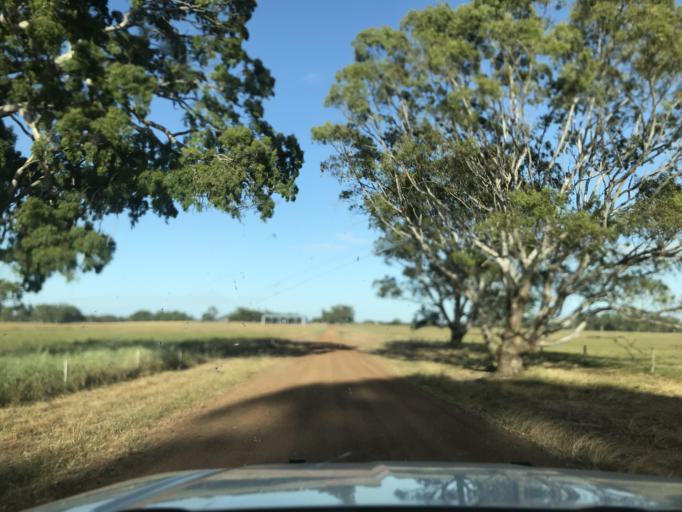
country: AU
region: South Australia
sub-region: Naracoorte and Lucindale
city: Naracoorte
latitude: -36.9555
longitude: 141.3655
